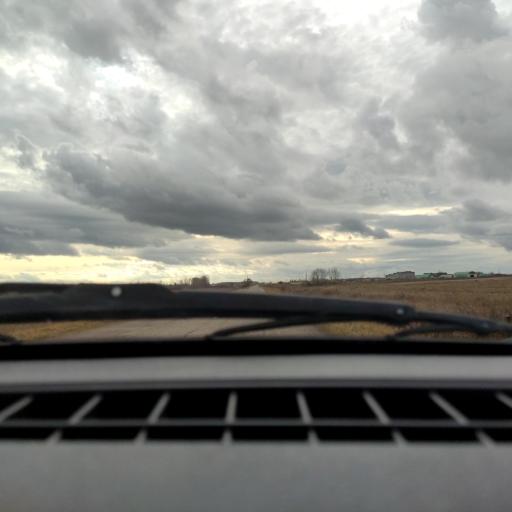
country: RU
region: Bashkortostan
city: Asanovo
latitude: 54.9175
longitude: 55.5068
